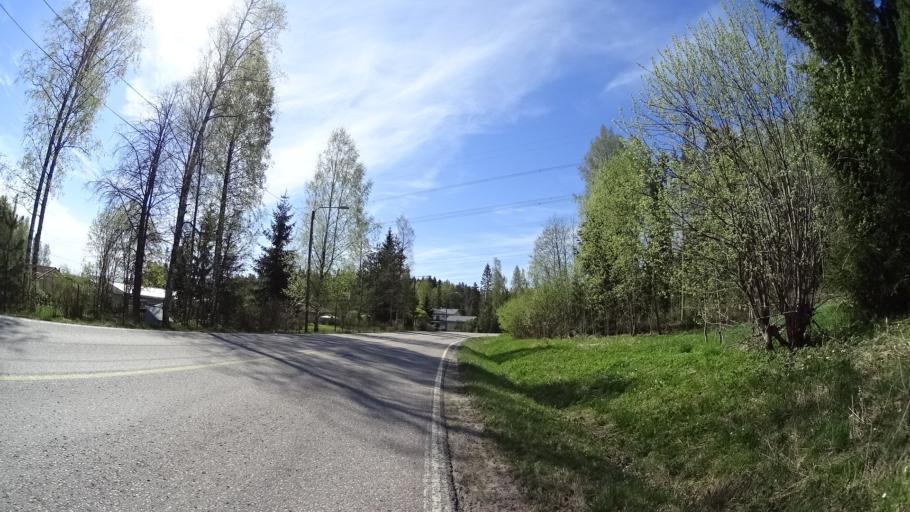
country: FI
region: Uusimaa
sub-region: Helsinki
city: Nurmijaervi
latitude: 60.3851
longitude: 24.8373
